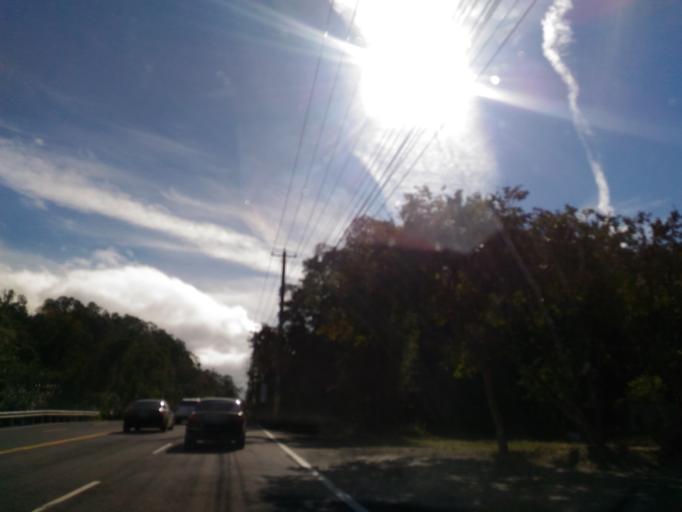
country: TW
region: Taiwan
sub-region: Hsinchu
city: Hsinchu
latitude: 24.7180
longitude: 121.0738
